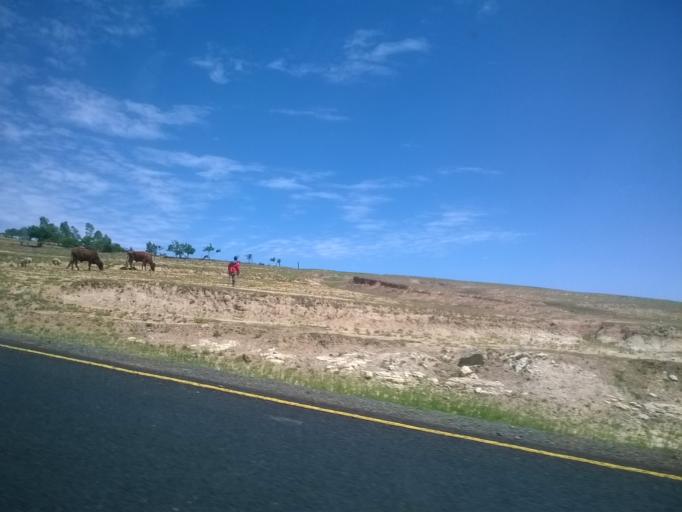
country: LS
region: Berea
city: Teyateyaneng
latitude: -29.1032
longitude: 27.8389
